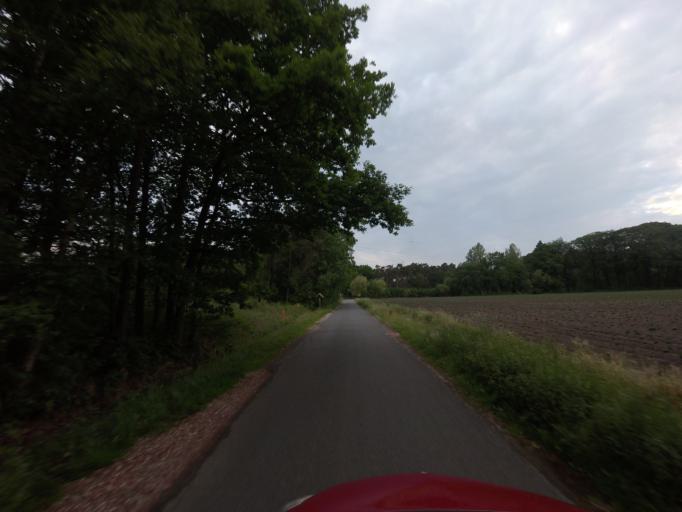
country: BE
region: Flanders
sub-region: Provincie Antwerpen
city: Zoersel
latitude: 51.2733
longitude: 4.7268
